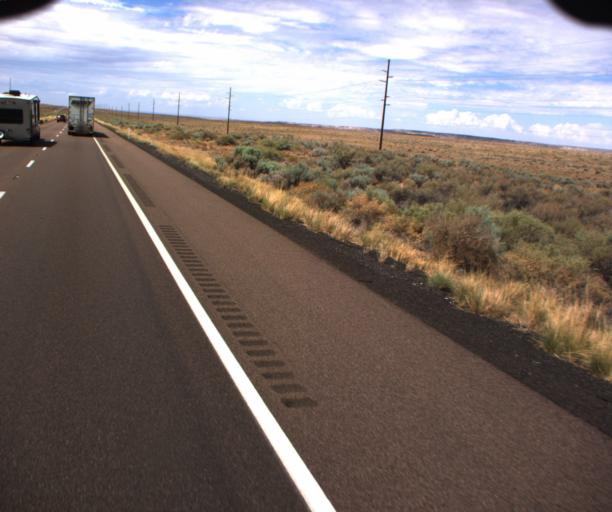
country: US
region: Arizona
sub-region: Navajo County
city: Holbrook
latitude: 35.0350
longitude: -109.8259
